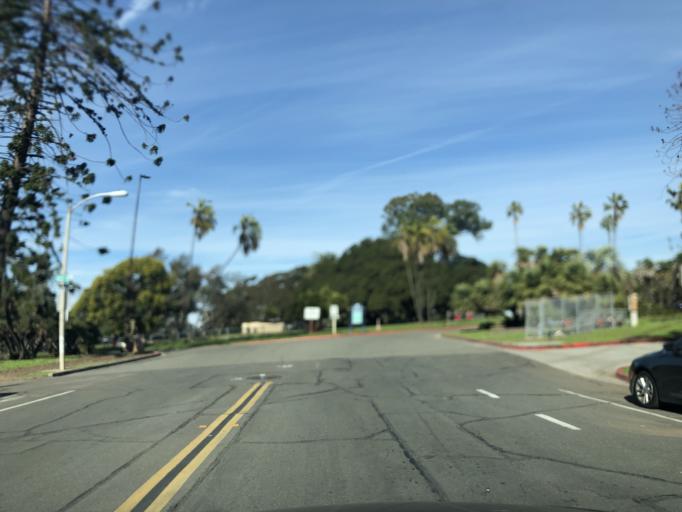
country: US
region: California
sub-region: San Diego County
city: San Diego
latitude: 32.7193
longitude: -117.1404
